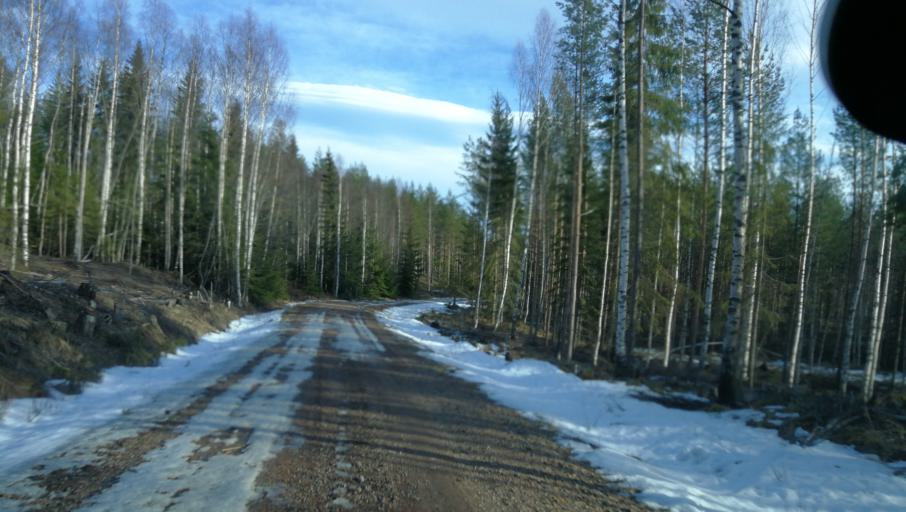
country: SE
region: Dalarna
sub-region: Vansbro Kommun
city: Vansbro
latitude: 60.7992
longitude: 14.2195
